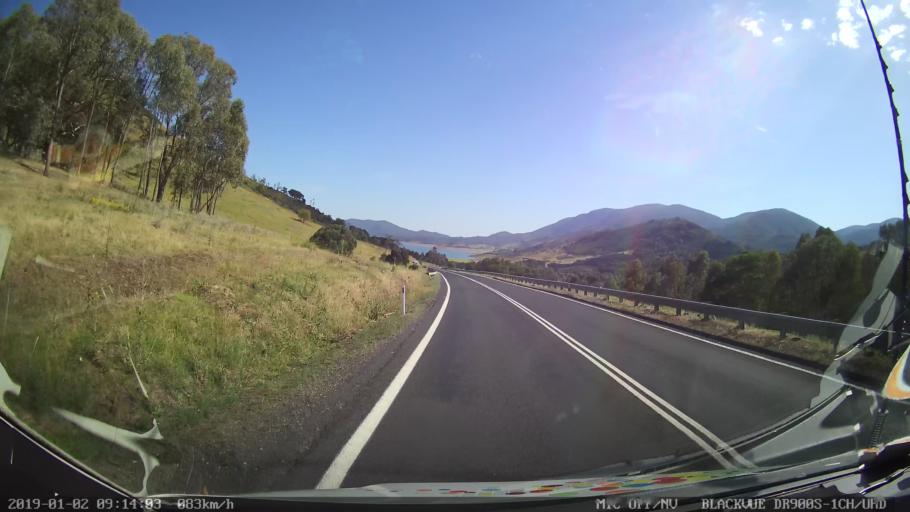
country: AU
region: New South Wales
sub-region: Tumut Shire
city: Tumut
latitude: -35.4821
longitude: 148.2723
